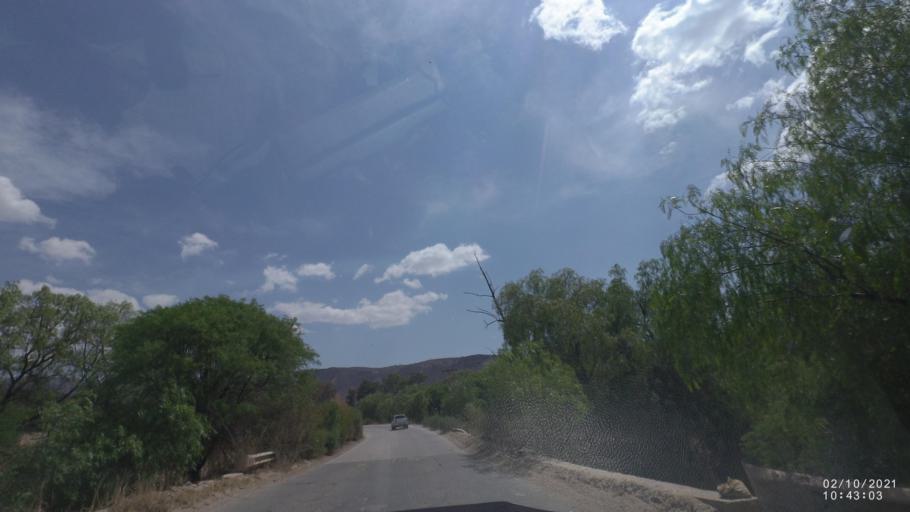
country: BO
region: Cochabamba
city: Capinota
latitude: -17.6012
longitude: -66.2976
